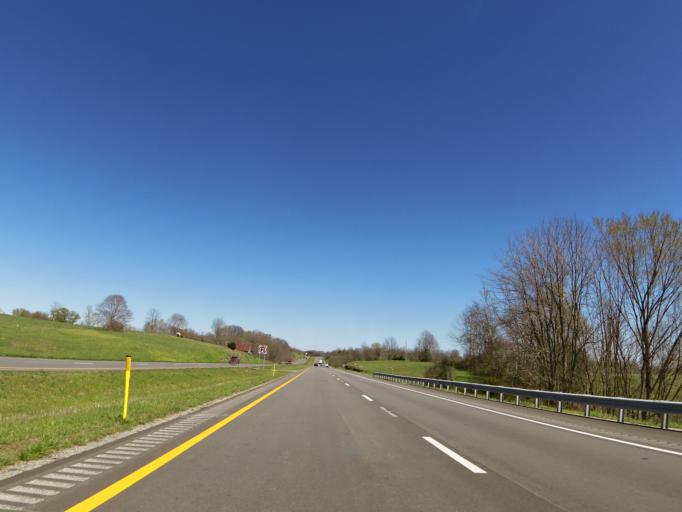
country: US
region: Kentucky
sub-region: Pulaski County
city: Somerset
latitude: 37.0971
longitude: -84.7458
